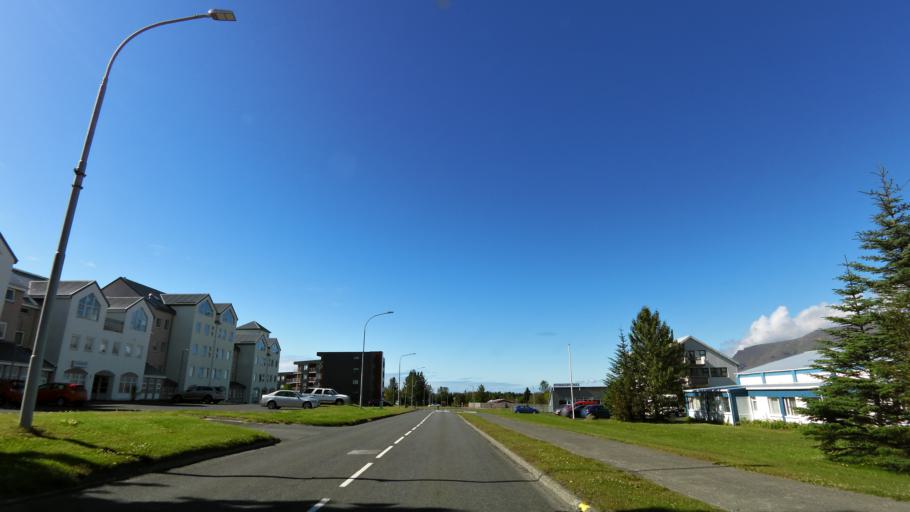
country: IS
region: Capital Region
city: Mosfellsbaer
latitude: 64.1678
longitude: -21.6996
